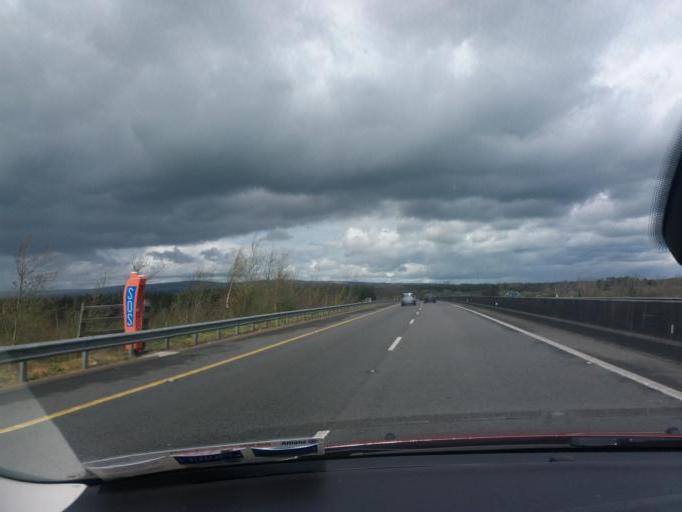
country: IE
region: Leinster
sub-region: Laois
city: Mountrath
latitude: 52.9800
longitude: -7.4324
